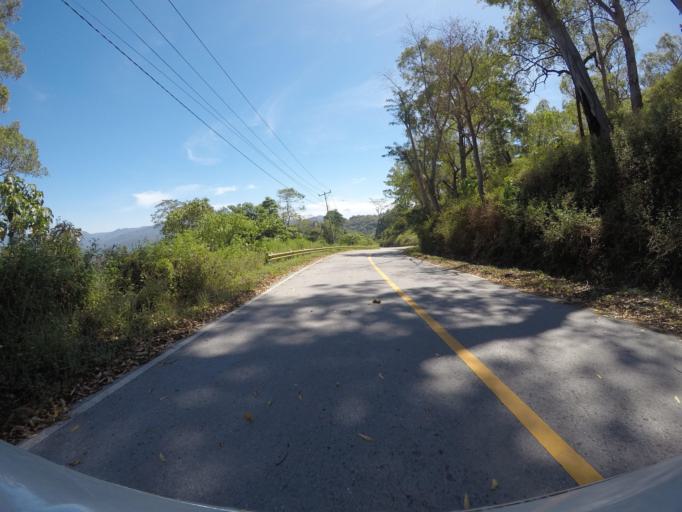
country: TL
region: Manufahi
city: Same
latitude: -8.8855
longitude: 125.9867
